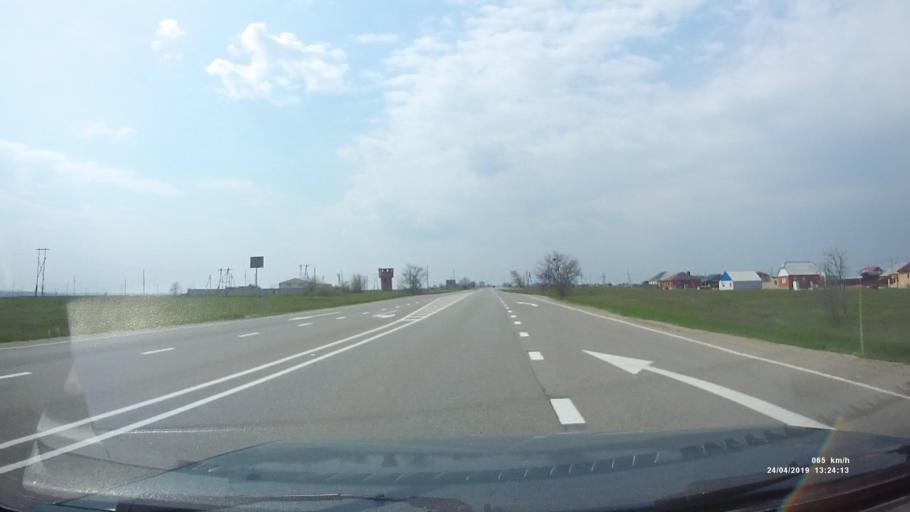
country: RU
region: Kalmykiya
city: Elista
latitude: 46.2839
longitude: 44.2589
